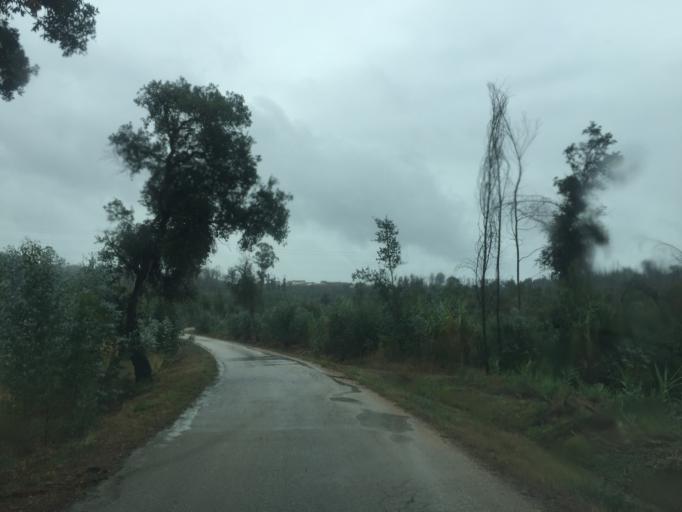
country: PT
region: Coimbra
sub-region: Figueira da Foz
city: Lavos
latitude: 40.0806
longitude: -8.7996
